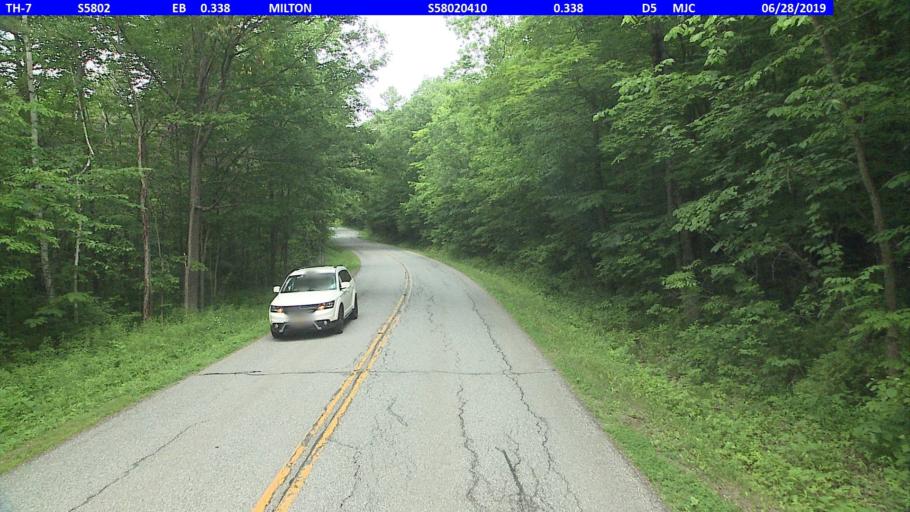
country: US
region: Vermont
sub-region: Chittenden County
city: Colchester
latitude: 44.6131
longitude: -73.2043
